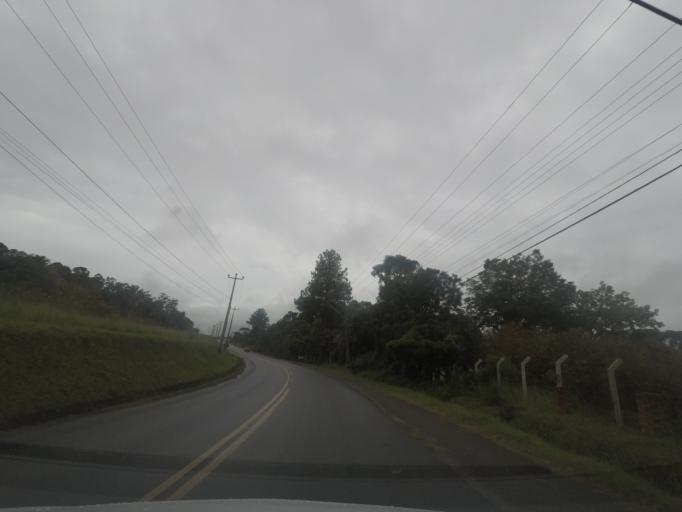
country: BR
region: Parana
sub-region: Campina Grande Do Sul
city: Campina Grande do Sul
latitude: -25.3243
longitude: -49.0785
